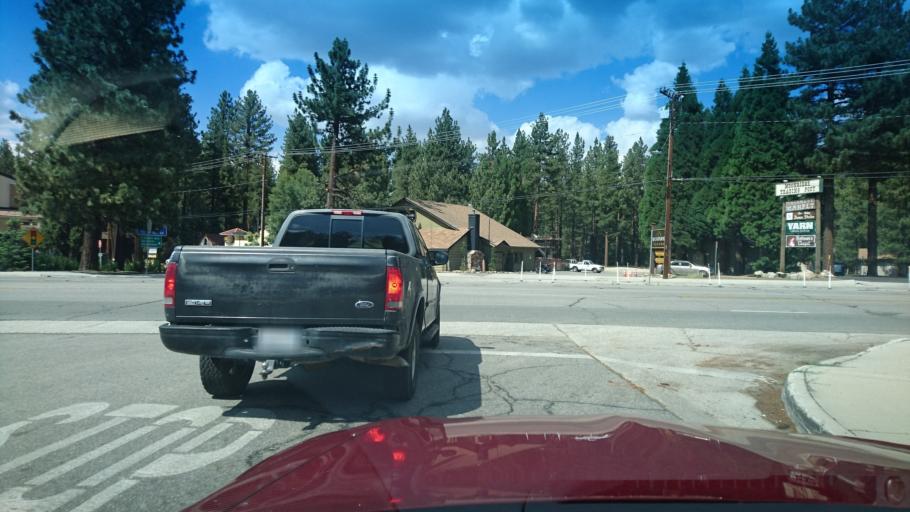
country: US
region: California
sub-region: San Bernardino County
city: Big Bear Lake
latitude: 34.2441
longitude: -116.8825
